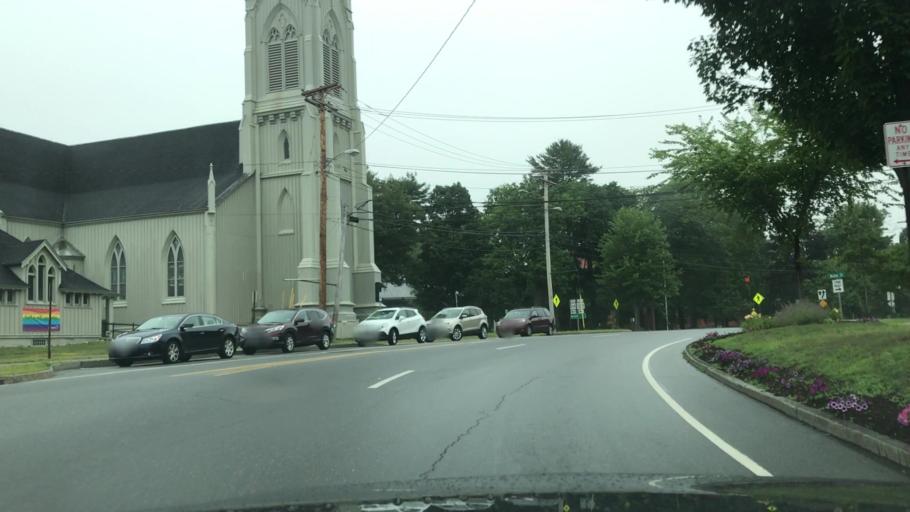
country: US
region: Maine
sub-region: Cumberland County
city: Brunswick
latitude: 43.9112
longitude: -69.9632
